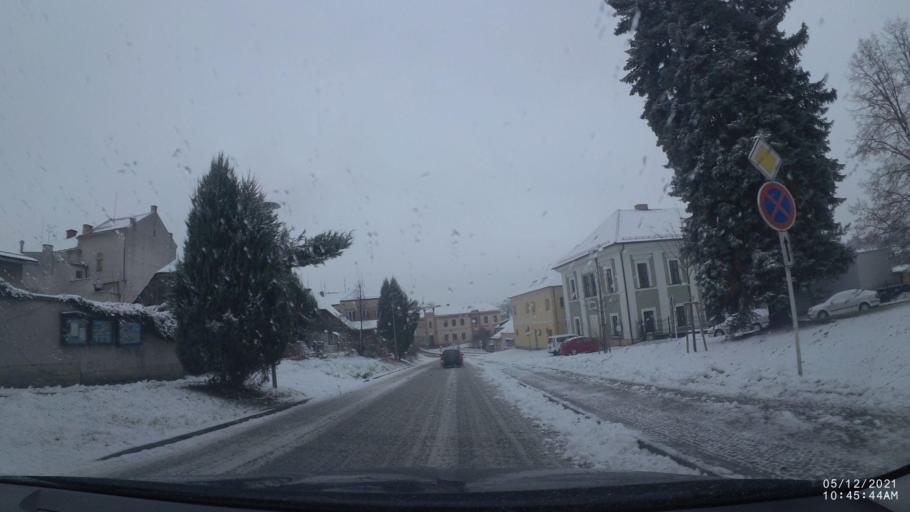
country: CZ
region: Kralovehradecky
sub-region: Okres Rychnov nad Kneznou
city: Rychnov nad Kneznou
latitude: 50.1652
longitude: 16.2751
